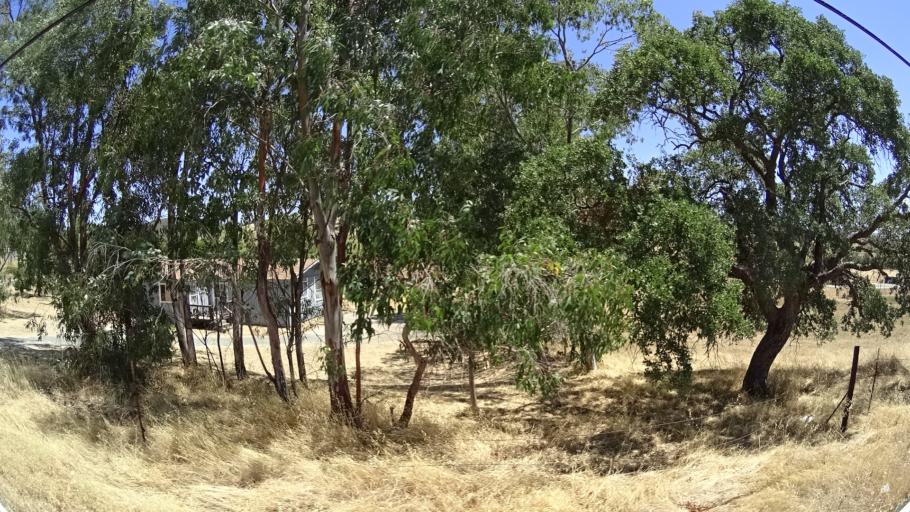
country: US
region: California
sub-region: Calaveras County
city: Valley Springs
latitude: 38.2255
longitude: -120.8206
